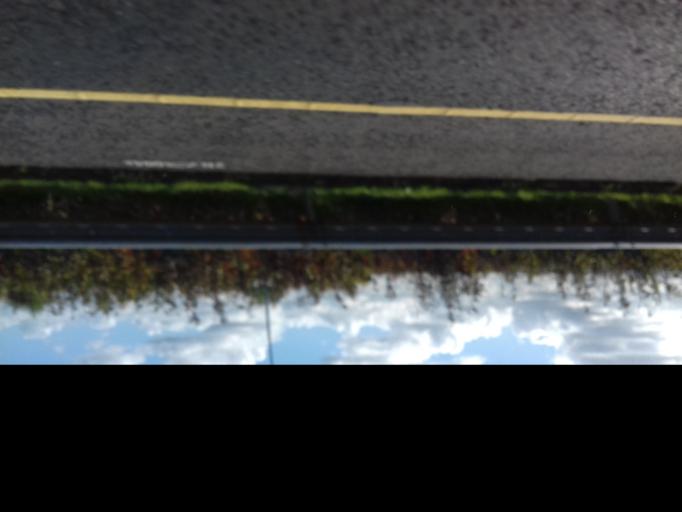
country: IE
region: Leinster
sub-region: Fingal County
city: Blanchardstown
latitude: 53.4342
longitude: -6.3488
